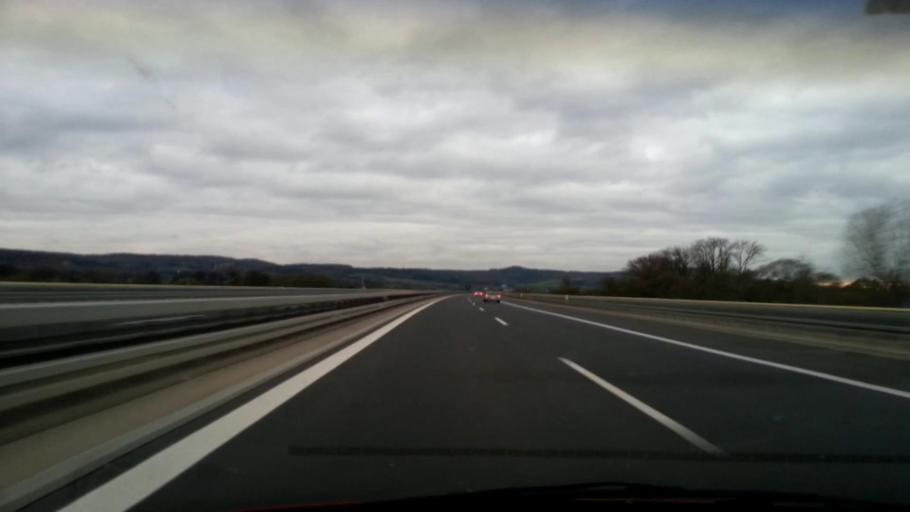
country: DE
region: Bavaria
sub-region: Upper Franconia
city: Lichtenfels
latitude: 50.1409
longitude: 11.0341
